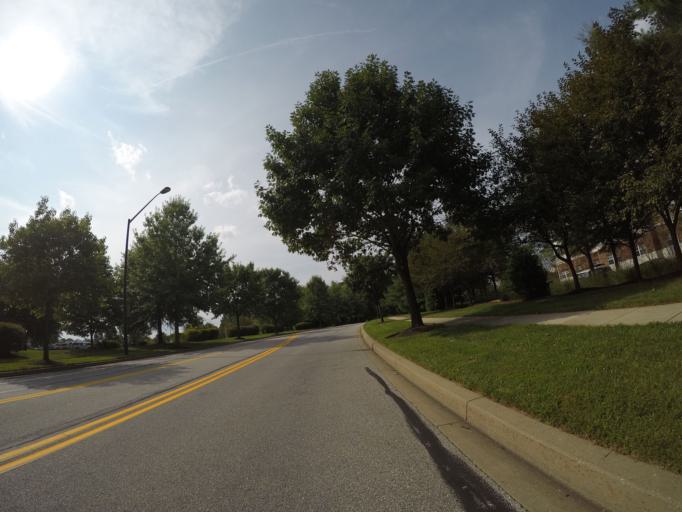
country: US
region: Maryland
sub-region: Howard County
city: Columbia
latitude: 39.3087
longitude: -76.8896
